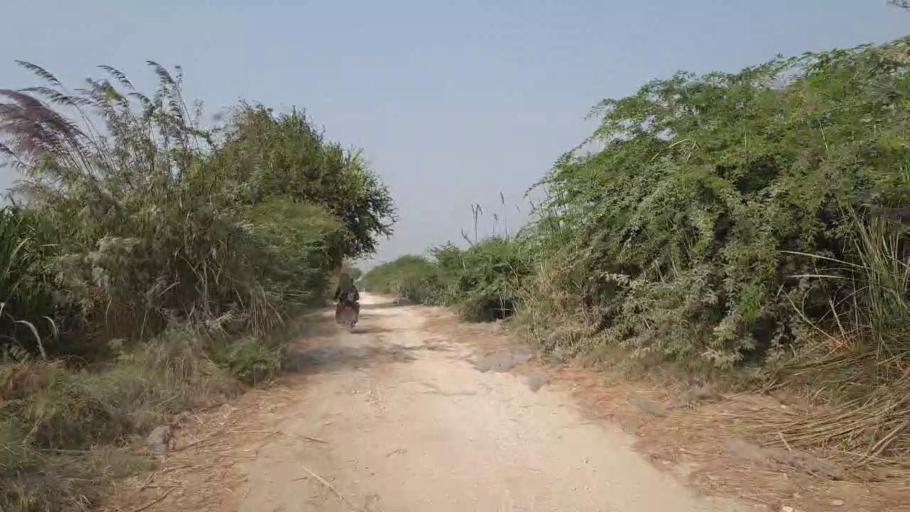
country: PK
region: Sindh
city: Matli
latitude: 25.0200
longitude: 68.5983
